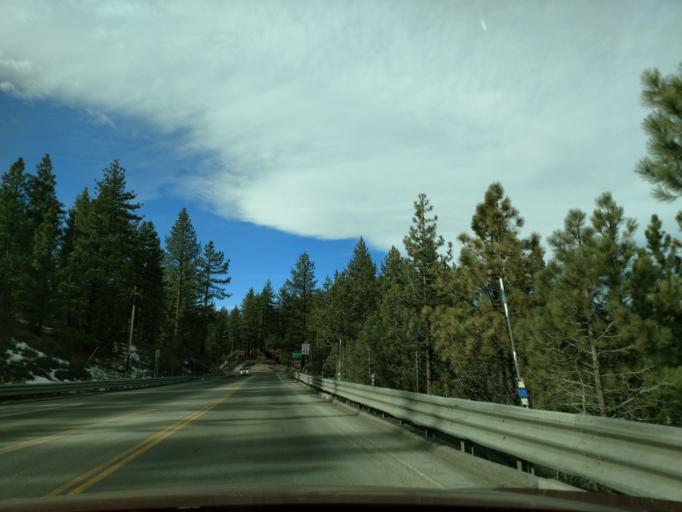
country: US
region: Nevada
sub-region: Douglas County
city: Kingsbury
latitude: 39.1027
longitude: -119.9131
